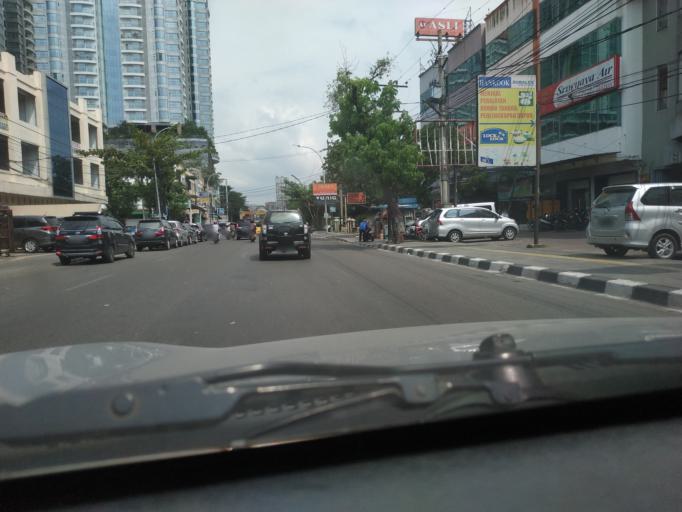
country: ID
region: North Sumatra
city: Medan
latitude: 3.5843
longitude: 98.6655
